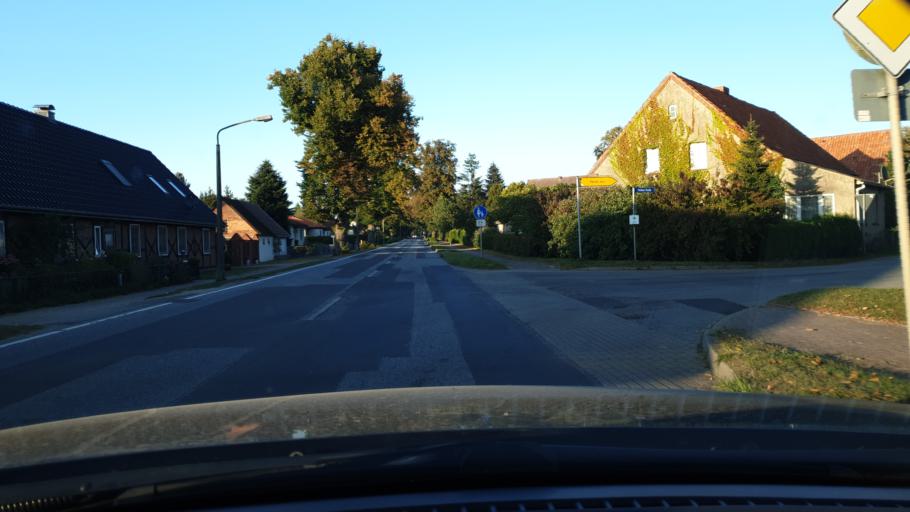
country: DE
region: Mecklenburg-Vorpommern
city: Wittenburg
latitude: 53.5777
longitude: 11.1051
